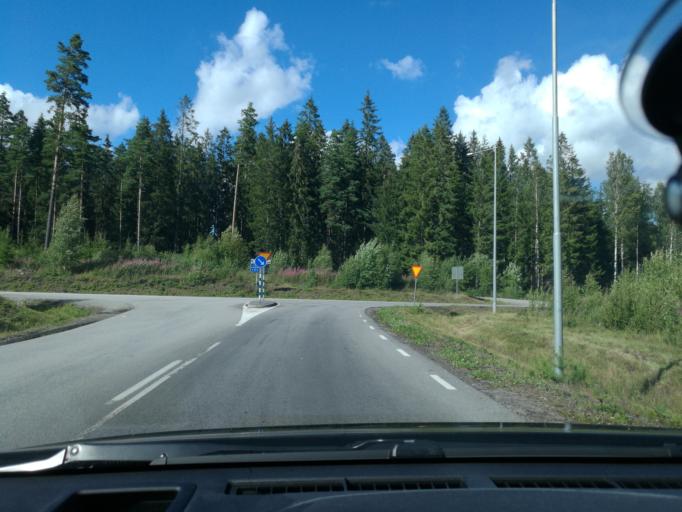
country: SE
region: Kronoberg
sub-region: Alvesta Kommun
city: Vislanda
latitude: 56.7941
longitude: 14.4566
